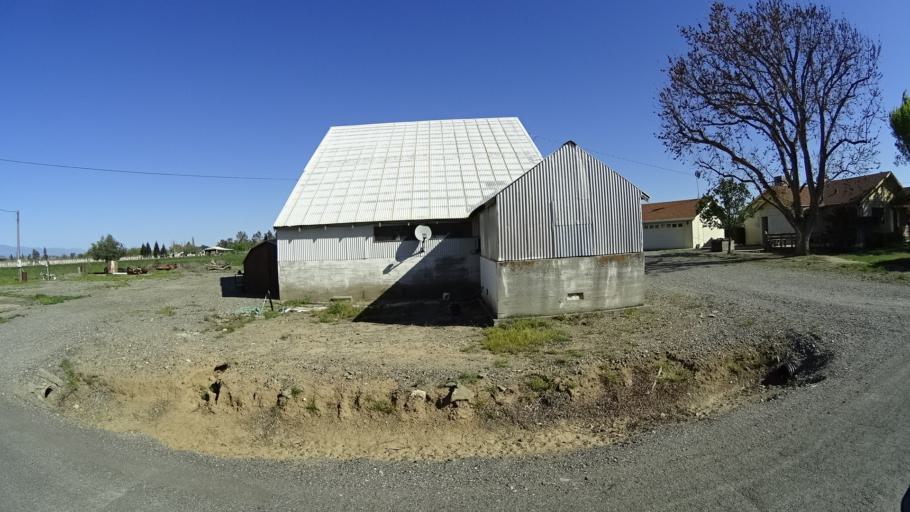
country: US
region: California
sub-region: Glenn County
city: Orland
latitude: 39.7369
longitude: -122.2239
